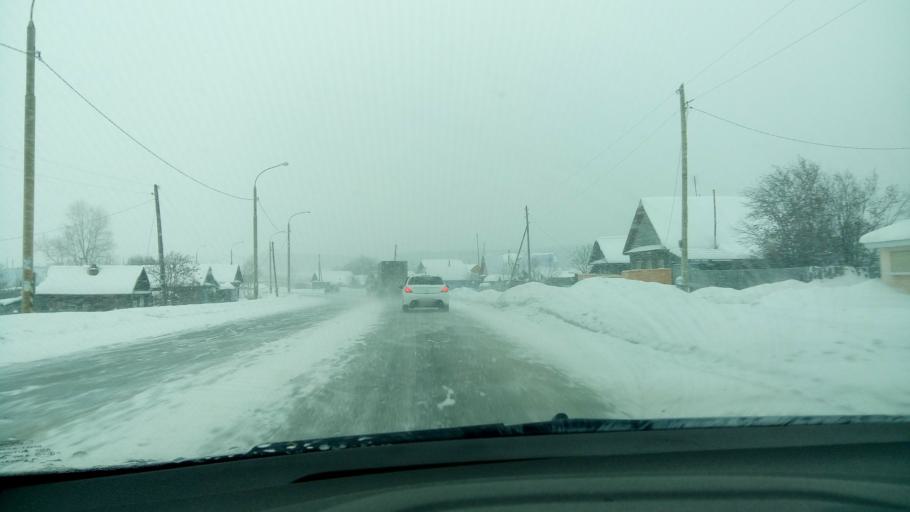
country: RU
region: Sverdlovsk
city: Beloyarskiy
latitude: 56.7699
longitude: 61.4577
